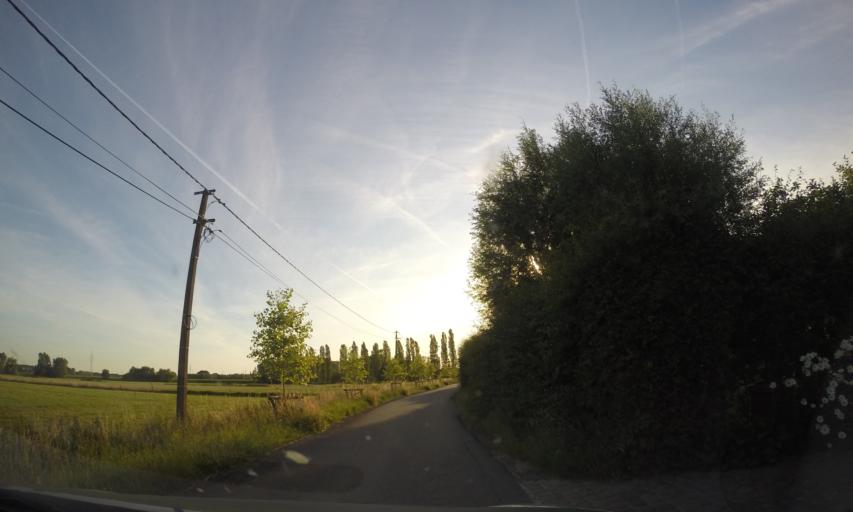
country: BE
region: Flanders
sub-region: Provincie Oost-Vlaanderen
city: Aalter
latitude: 51.1182
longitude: 3.4866
